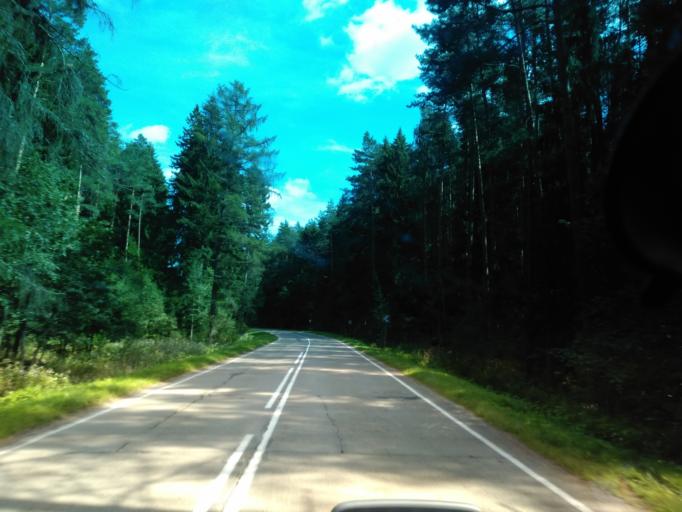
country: BY
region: Minsk
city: Stan'kava
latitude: 53.6212
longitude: 27.3101
